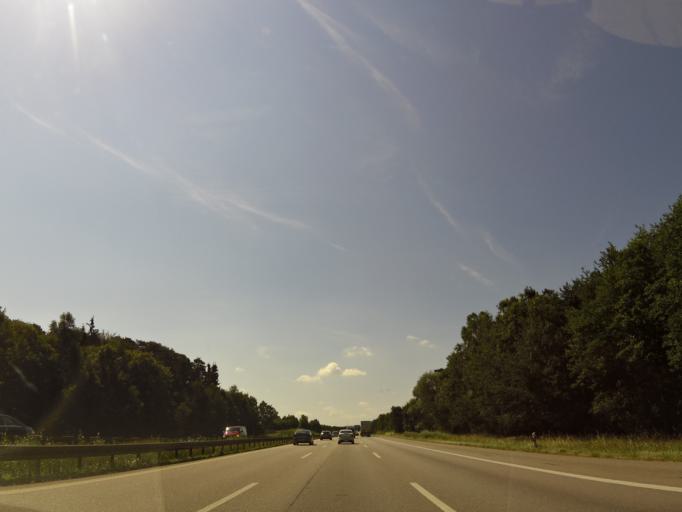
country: DE
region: Bavaria
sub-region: Upper Bavaria
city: Reichertshofen
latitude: 48.6627
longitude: 11.5110
